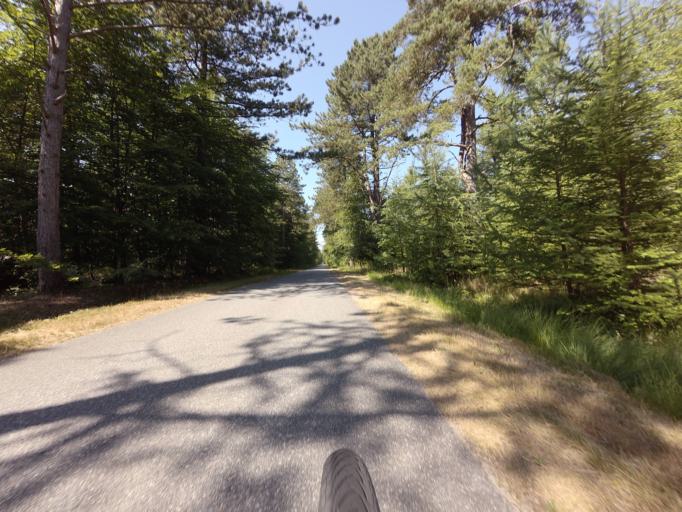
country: DK
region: North Denmark
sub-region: Laeso Kommune
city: Byrum
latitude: 57.2897
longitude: 11.0047
